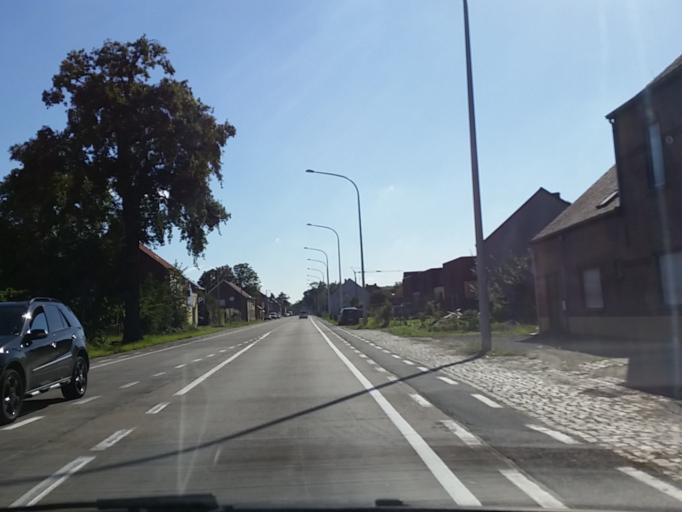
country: BE
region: Flanders
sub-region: Provincie Vlaams-Brabant
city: Haacht
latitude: 50.9400
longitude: 4.6175
